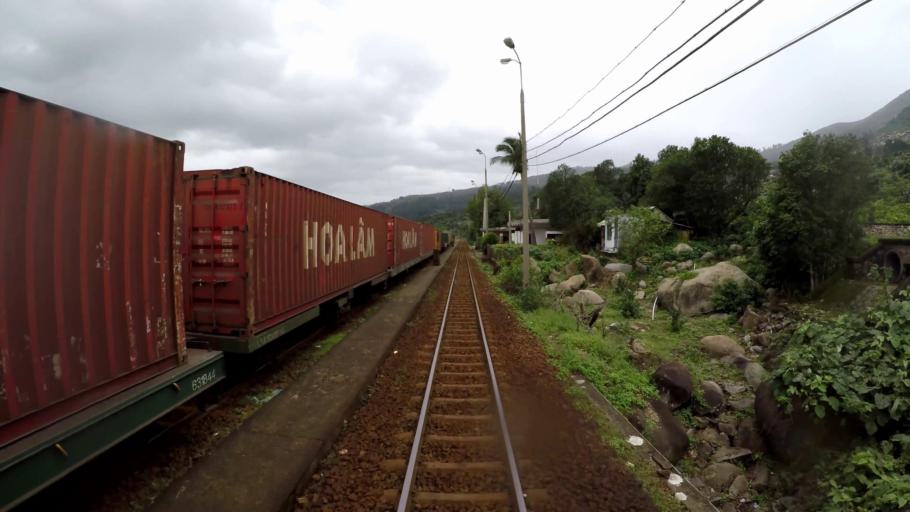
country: VN
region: Da Nang
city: Lien Chieu
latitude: 16.1675
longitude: 108.1359
